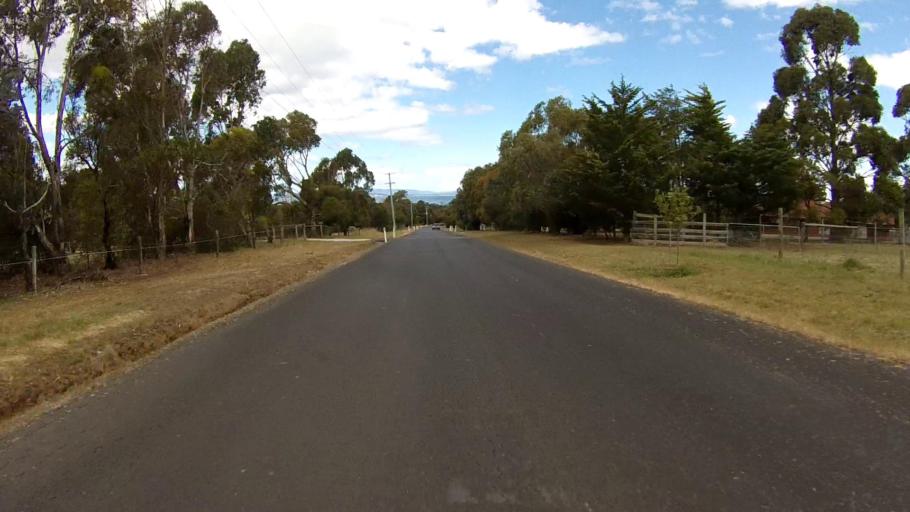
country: AU
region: Tasmania
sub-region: Clarence
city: Acton Park
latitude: -42.8821
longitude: 147.4760
